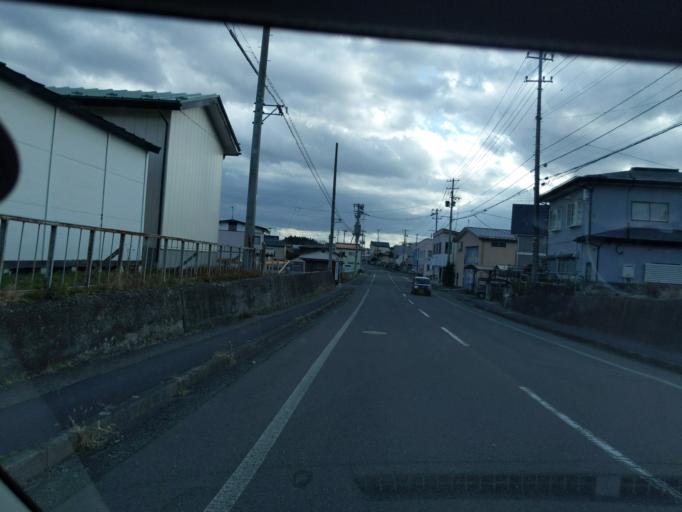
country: JP
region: Iwate
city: Mizusawa
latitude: 39.1315
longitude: 141.1412
